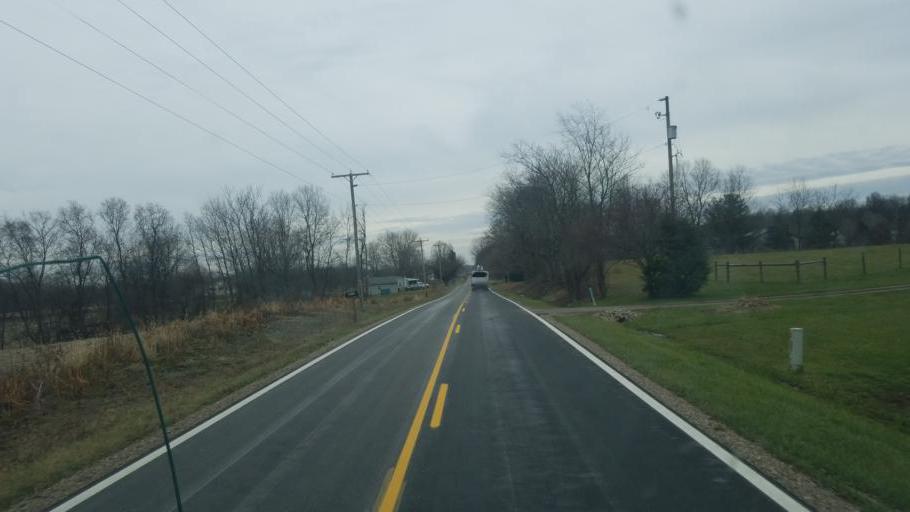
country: US
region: Ohio
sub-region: Licking County
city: Utica
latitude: 40.2607
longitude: -82.5666
